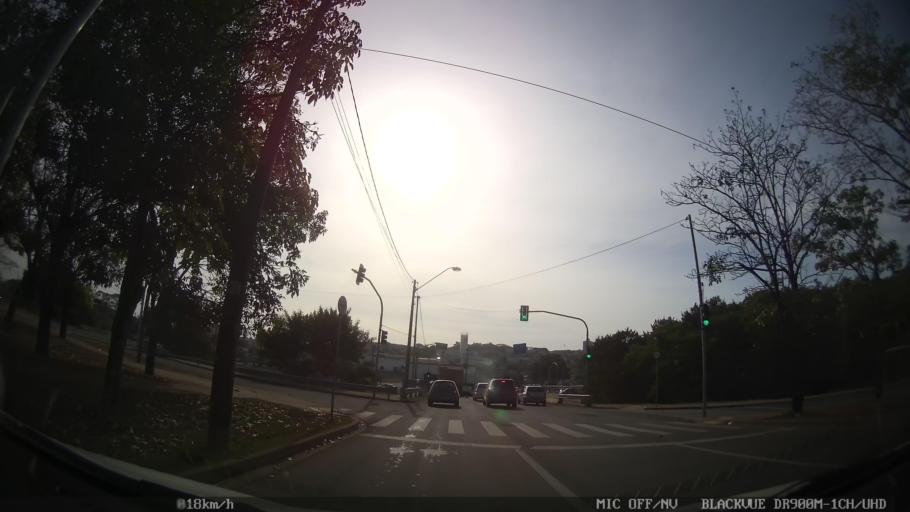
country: BR
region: Sao Paulo
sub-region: Piracicaba
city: Piracicaba
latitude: -22.7421
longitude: -47.6687
